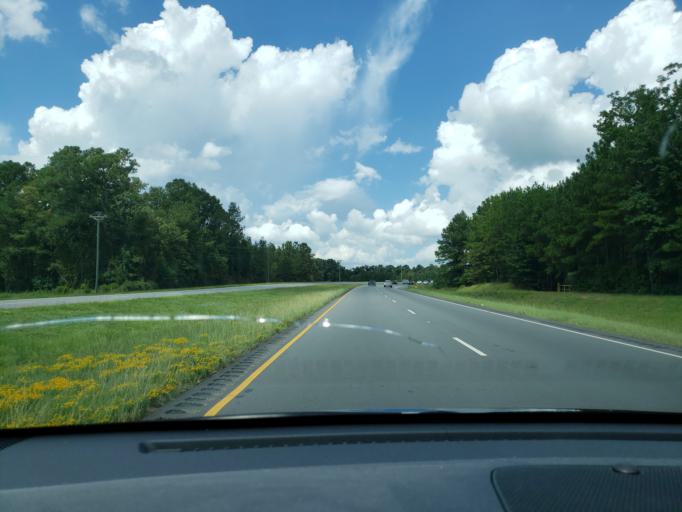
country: US
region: North Carolina
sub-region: Robeson County
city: Saint Pauls
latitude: 34.7662
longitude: -78.8093
